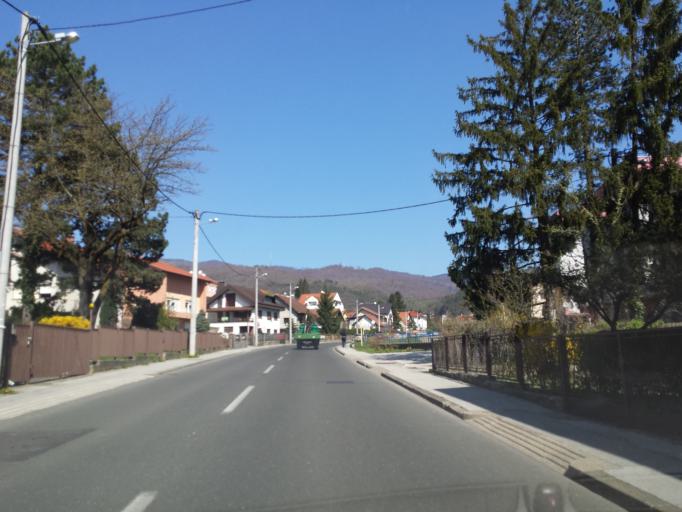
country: HR
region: Grad Zagreb
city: Zagreb
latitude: 45.8512
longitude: 15.9750
